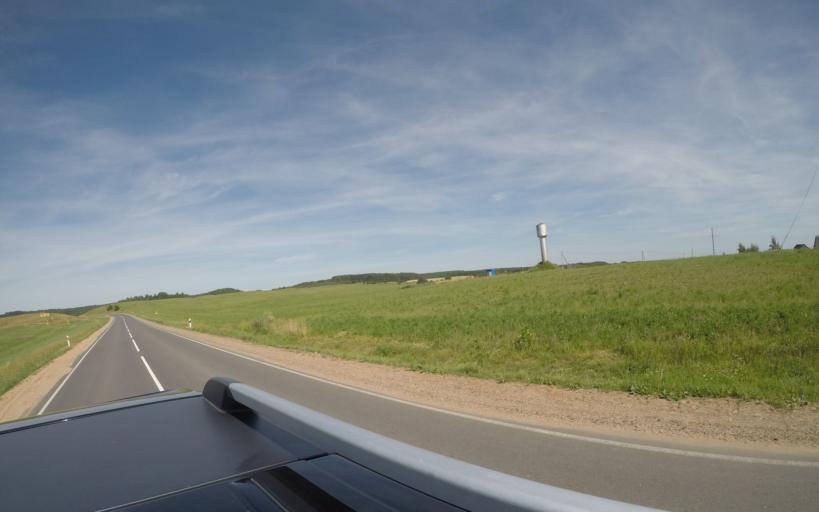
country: BY
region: Grodnenskaya
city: Hal'shany
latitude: 54.2620
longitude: 26.0210
